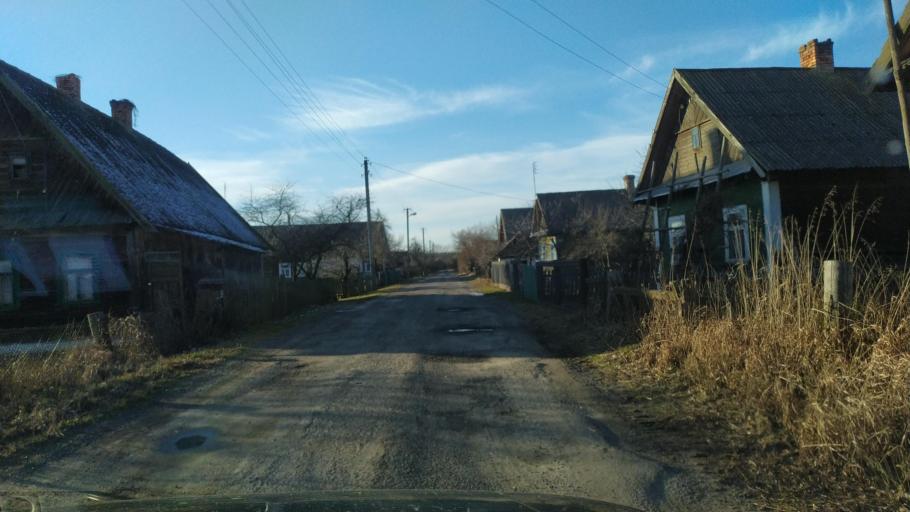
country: BY
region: Brest
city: Pruzhany
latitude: 52.5510
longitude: 24.2936
